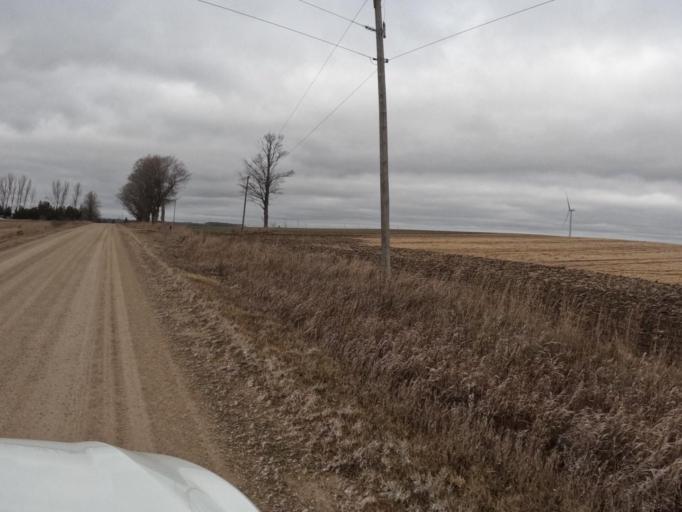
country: CA
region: Ontario
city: Shelburne
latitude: 44.0288
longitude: -80.3708
